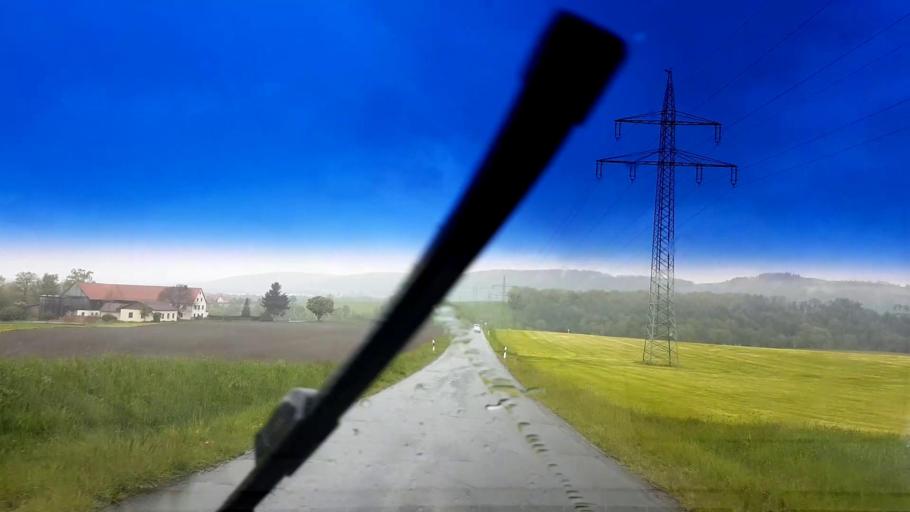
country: DE
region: Bavaria
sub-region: Upper Franconia
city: Gesees
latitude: 50.0273
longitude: 11.6276
